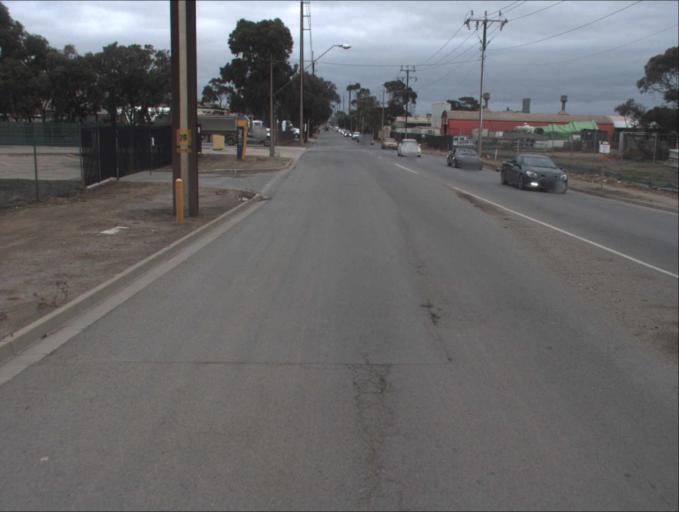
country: AU
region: South Australia
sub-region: Port Adelaide Enfield
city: Enfield
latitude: -34.8328
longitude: 138.5928
